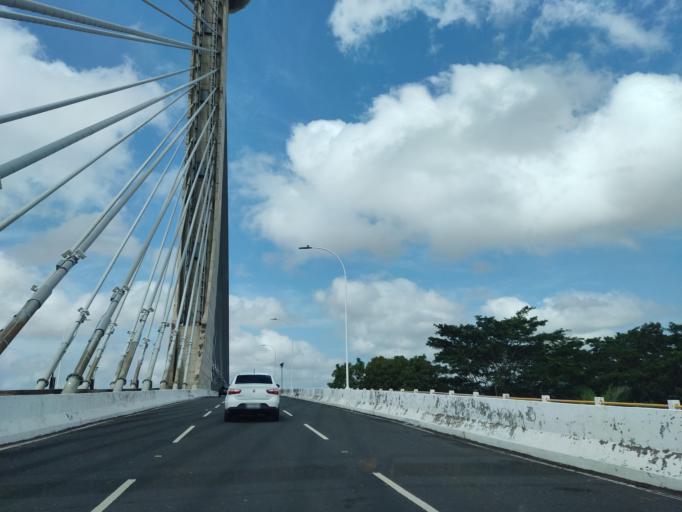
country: BR
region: Piaui
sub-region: Teresina
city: Teresina
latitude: -5.0696
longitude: -42.8018
